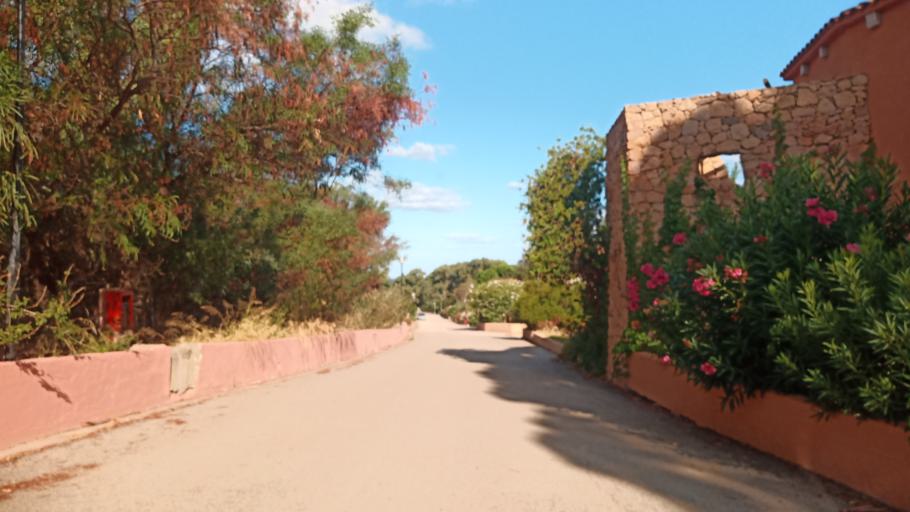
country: IT
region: Sardinia
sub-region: Provincia di Olbia-Tempio
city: Trinita d'Agultu
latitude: 41.0225
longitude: 8.8973
